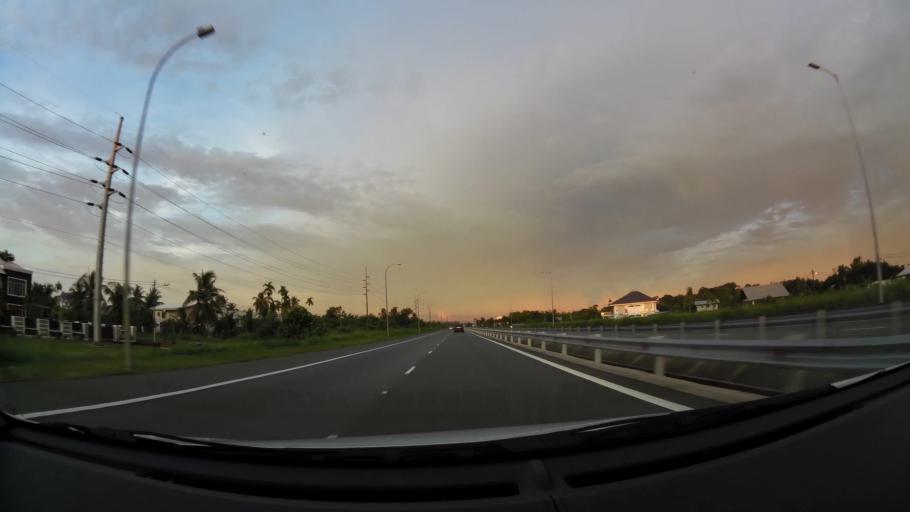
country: BN
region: Belait
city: Kuala Belait
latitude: 4.5805
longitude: 114.2445
